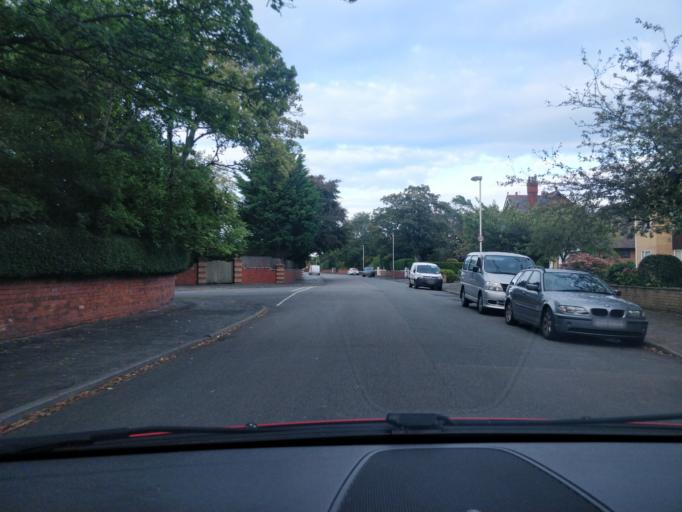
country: GB
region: England
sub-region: Sefton
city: Southport
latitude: 53.6526
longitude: -2.9836
